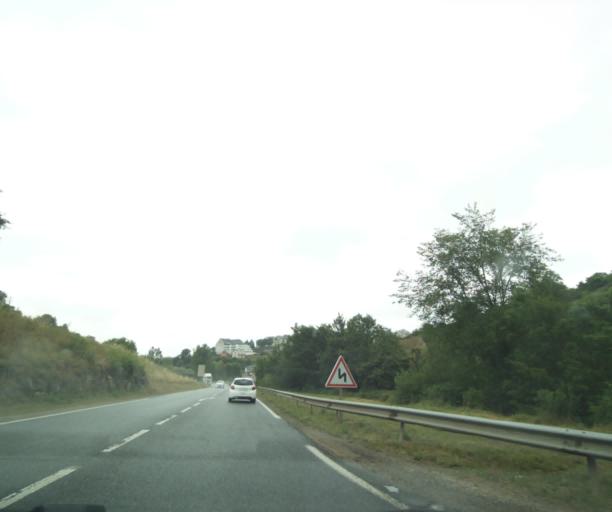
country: FR
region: Midi-Pyrenees
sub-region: Departement de l'Aveyron
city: Rodez
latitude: 44.3563
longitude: 2.5623
